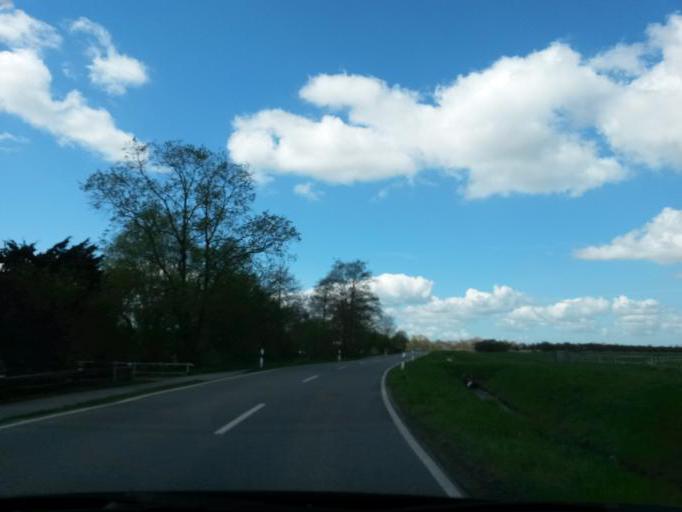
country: DE
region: Schleswig-Holstein
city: Neuendeich
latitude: 53.6742
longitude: 9.6273
